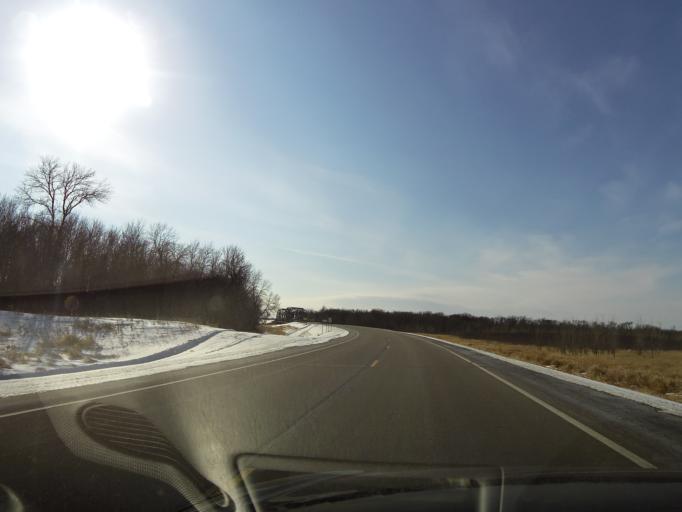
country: US
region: North Dakota
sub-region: Walsh County
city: Grafton
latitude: 48.4145
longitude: -97.1330
